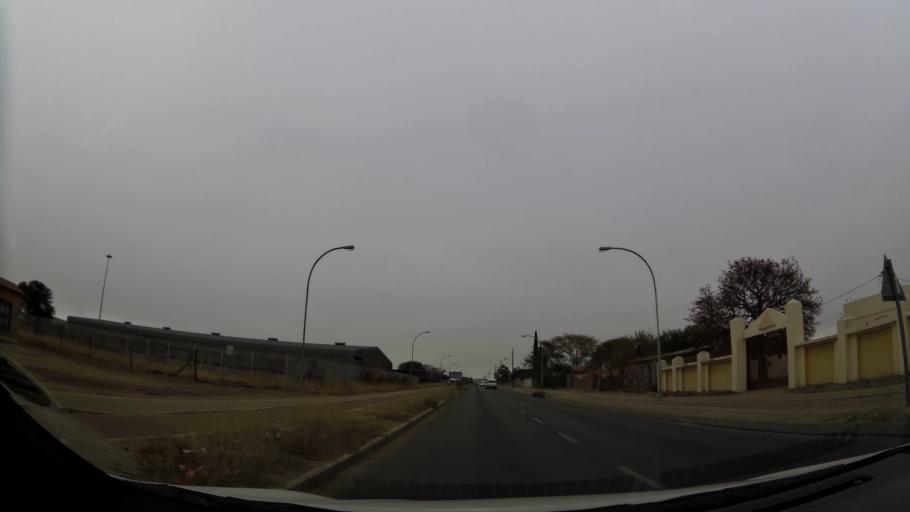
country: ZA
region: Limpopo
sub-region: Capricorn District Municipality
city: Polokwane
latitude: -23.8485
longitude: 29.3984
